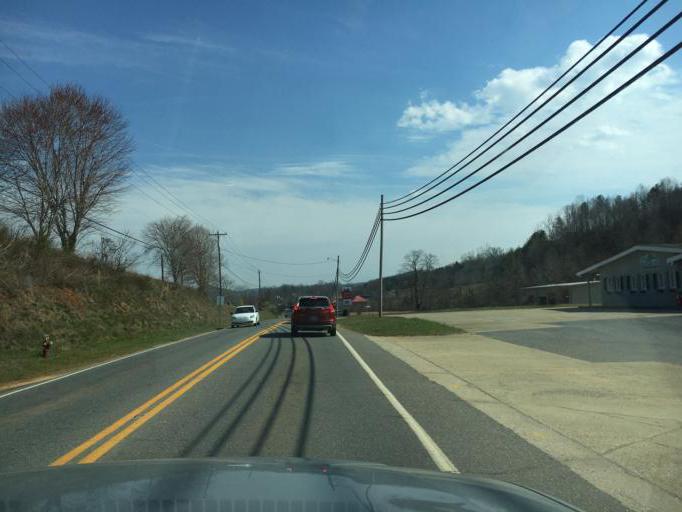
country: US
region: North Carolina
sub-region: McDowell County
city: Marion
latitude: 35.6706
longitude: -81.9851
